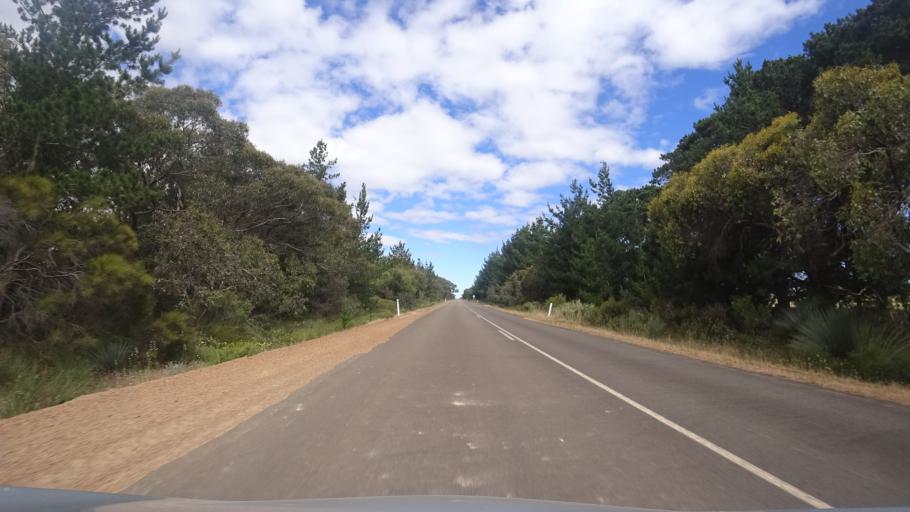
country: AU
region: South Australia
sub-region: Kangaroo Island
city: Kingscote
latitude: -35.7958
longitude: 137.0431
